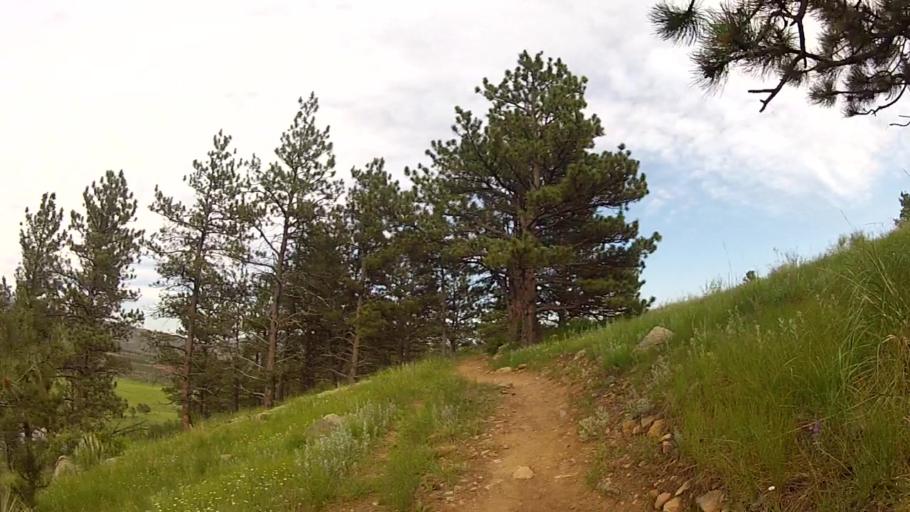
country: US
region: Colorado
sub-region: Larimer County
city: Laporte
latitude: 40.4878
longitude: -105.2407
